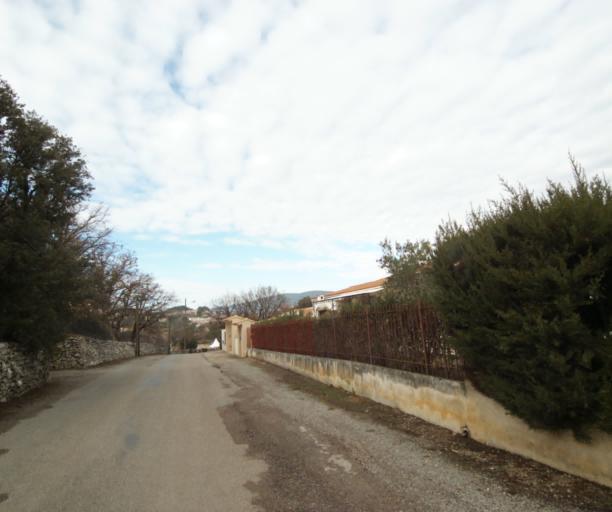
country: FR
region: Provence-Alpes-Cote d'Azur
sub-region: Departement du Var
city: Trans-en-Provence
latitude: 43.5200
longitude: 6.4855
